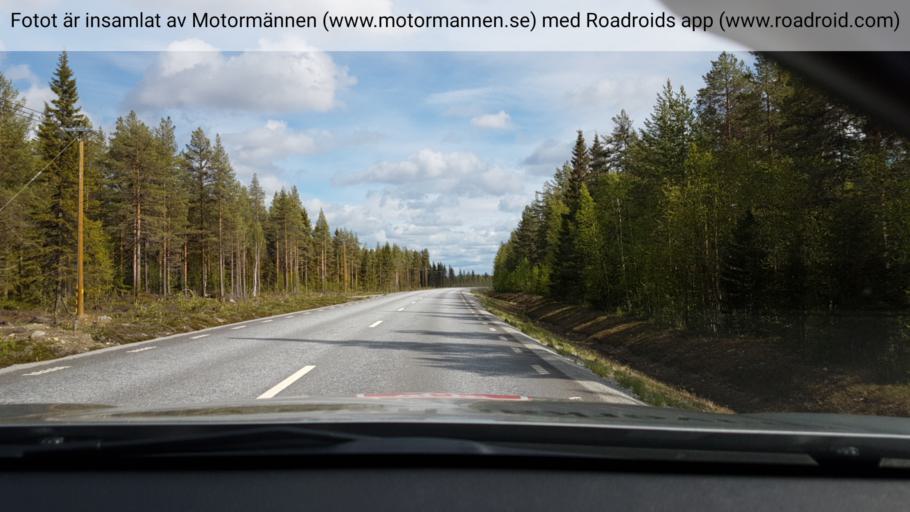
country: SE
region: Vaesterbotten
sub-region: Asele Kommun
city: Insjon
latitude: 64.1275
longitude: 18.0763
